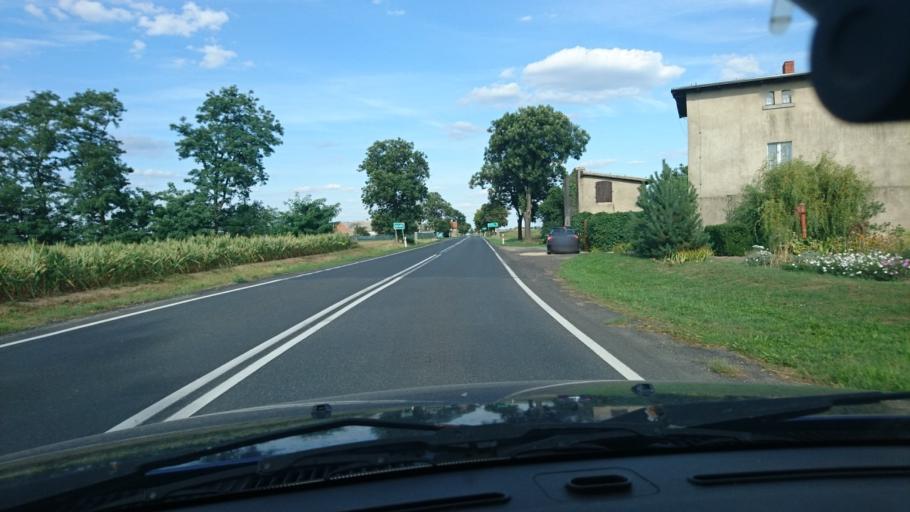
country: PL
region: Greater Poland Voivodeship
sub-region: Powiat krotoszynski
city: Kobylin
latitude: 51.7200
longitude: 17.2551
